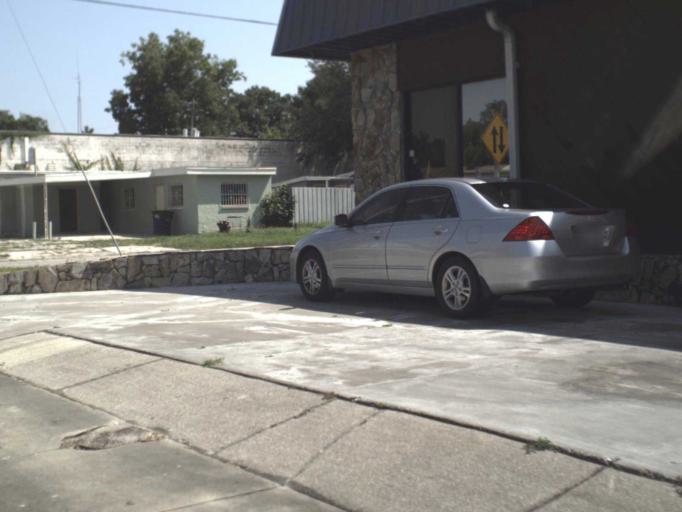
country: US
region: Florida
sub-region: Hillsborough County
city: Tampa
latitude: 27.9904
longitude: -82.4594
